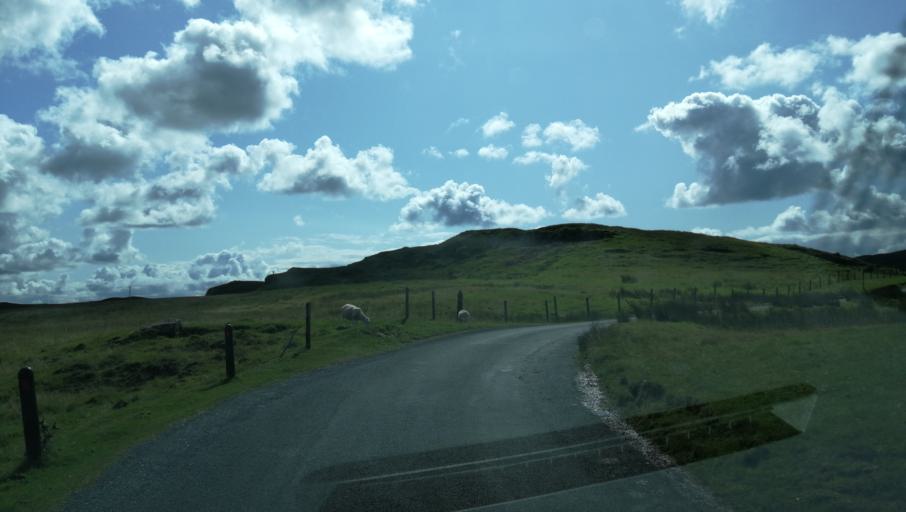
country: GB
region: Scotland
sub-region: Highland
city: Isle of Skye
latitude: 57.4259
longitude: -6.5801
